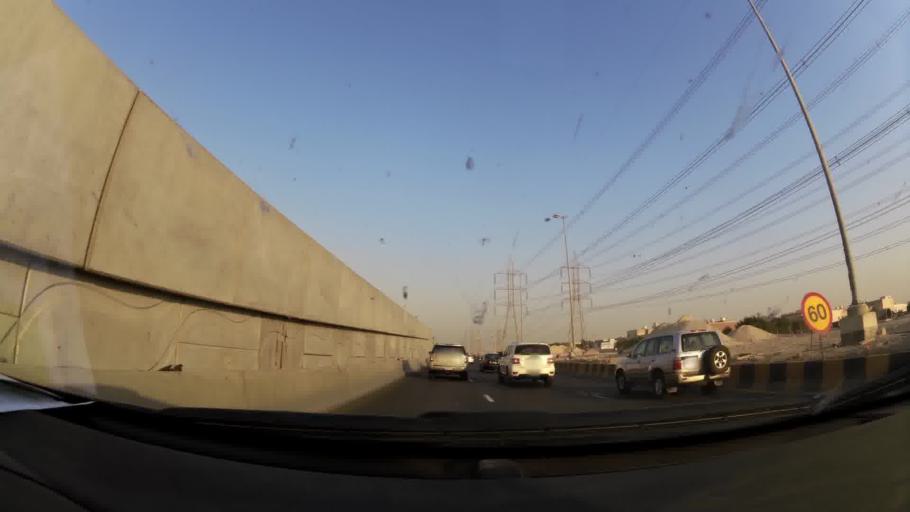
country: KW
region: Al Asimah
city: Ar Rabiyah
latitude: 29.2956
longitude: 47.8704
